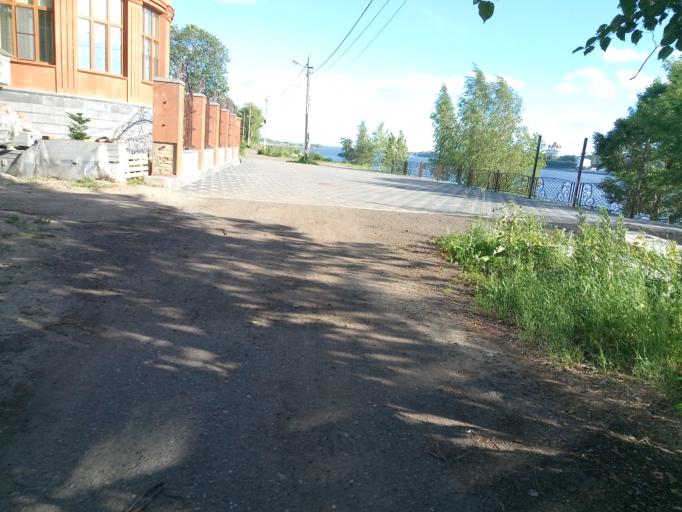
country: RU
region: Jaroslavl
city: Yaroslavl
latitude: 57.6352
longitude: 39.9044
